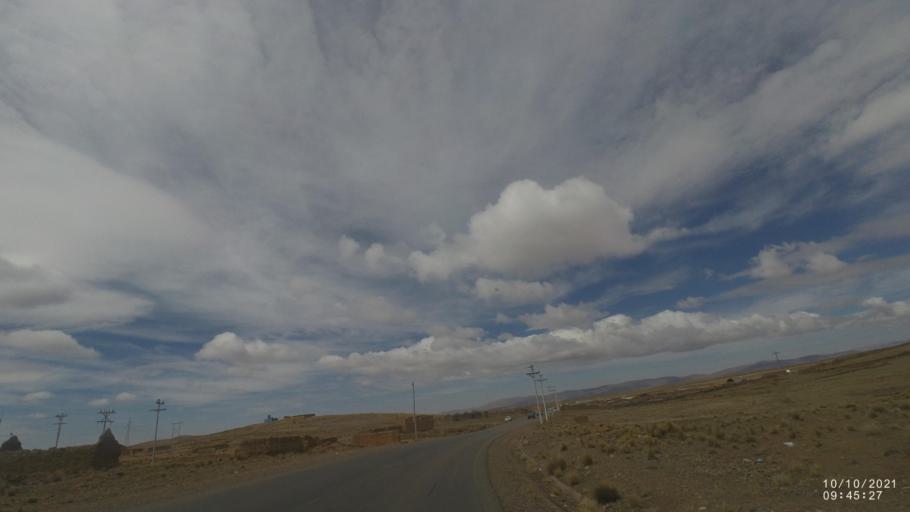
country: BO
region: La Paz
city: Quime
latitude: -17.1712
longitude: -67.3355
